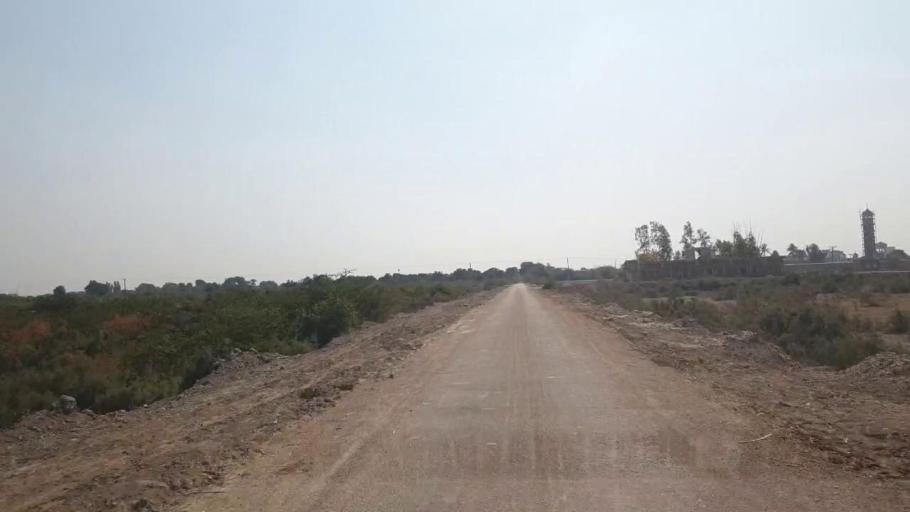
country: PK
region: Sindh
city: Chambar
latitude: 25.3779
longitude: 68.8808
